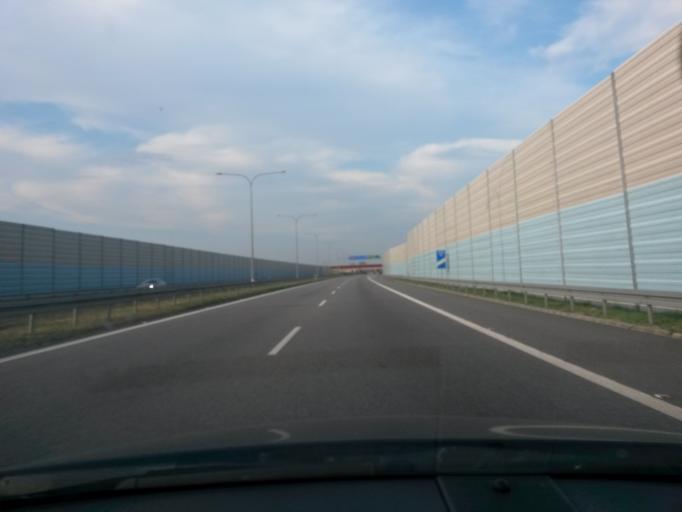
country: PL
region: Lodz Voivodeship
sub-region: powiat Lowicki
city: Lyszkowice
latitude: 51.9846
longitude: 19.8900
